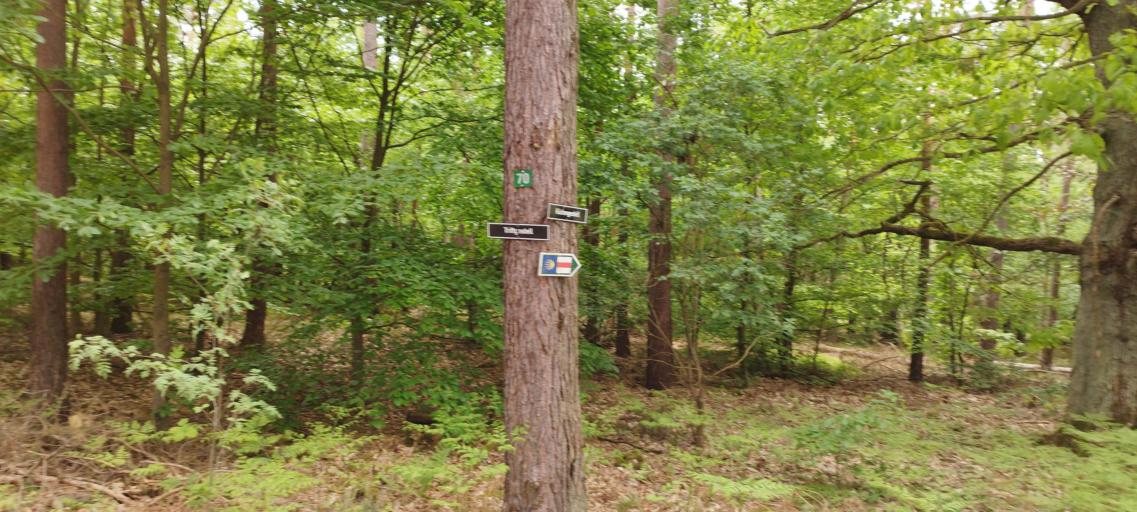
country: DE
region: Brandenburg
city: Rauen
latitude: 52.3768
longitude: 13.9675
